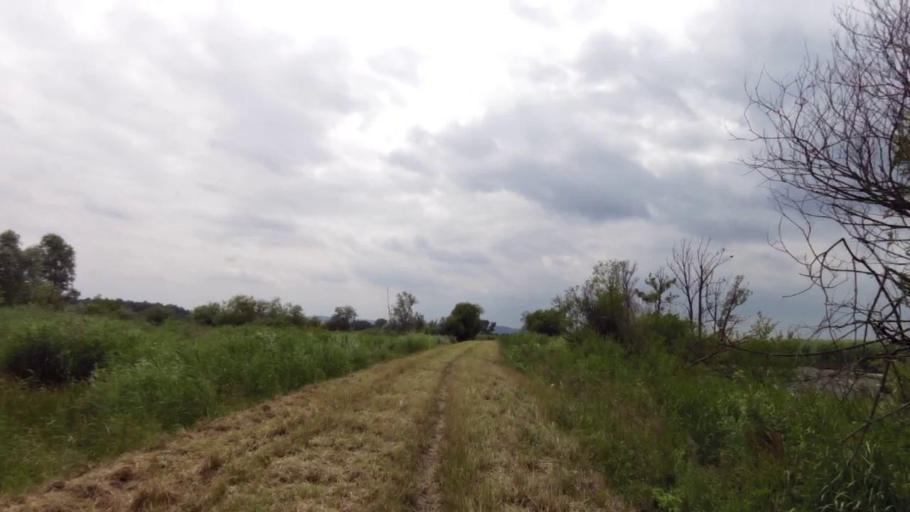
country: PL
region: West Pomeranian Voivodeship
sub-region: Szczecin
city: Szczecin
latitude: 53.4230
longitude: 14.6549
